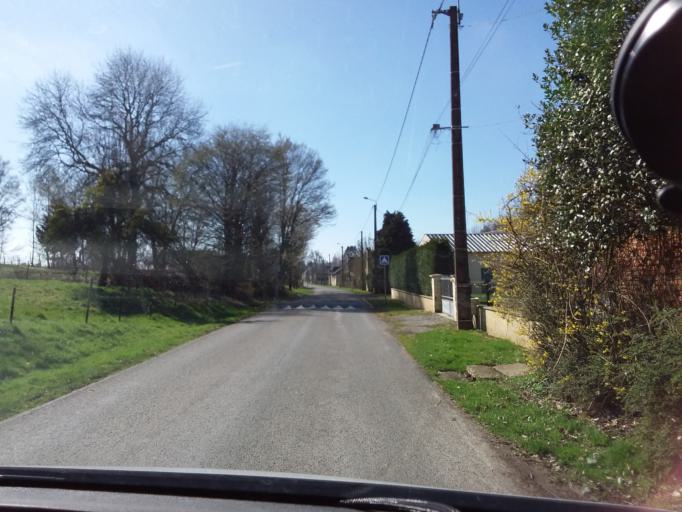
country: FR
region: Picardie
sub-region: Departement de l'Aisne
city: Montcornet
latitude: 49.7583
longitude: 4.0031
